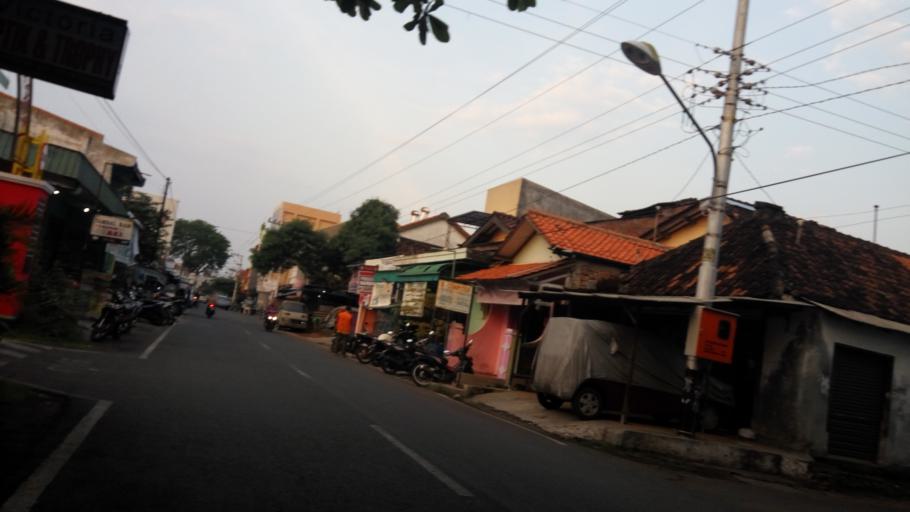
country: ID
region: Central Java
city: Semarang
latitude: -6.9857
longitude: 110.4055
